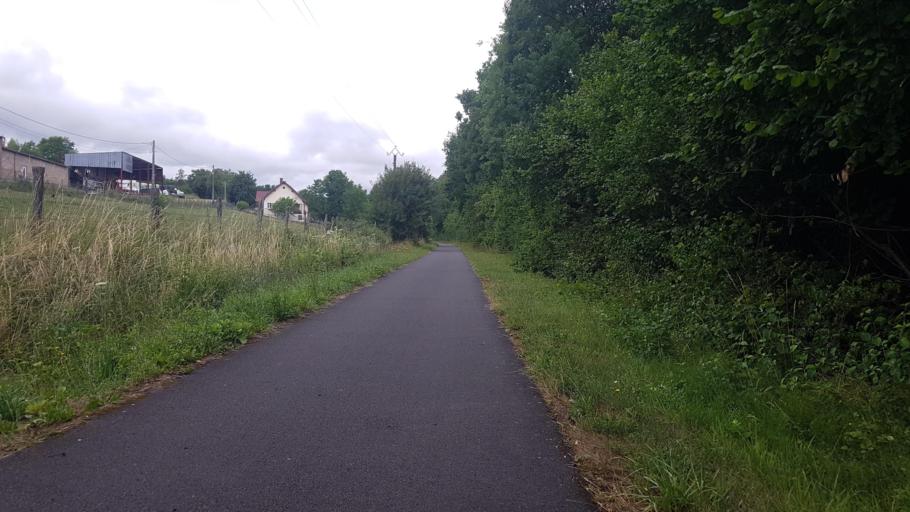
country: FR
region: Lorraine
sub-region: Departement de la Moselle
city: Sarrebourg
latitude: 48.7052
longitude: 7.0227
